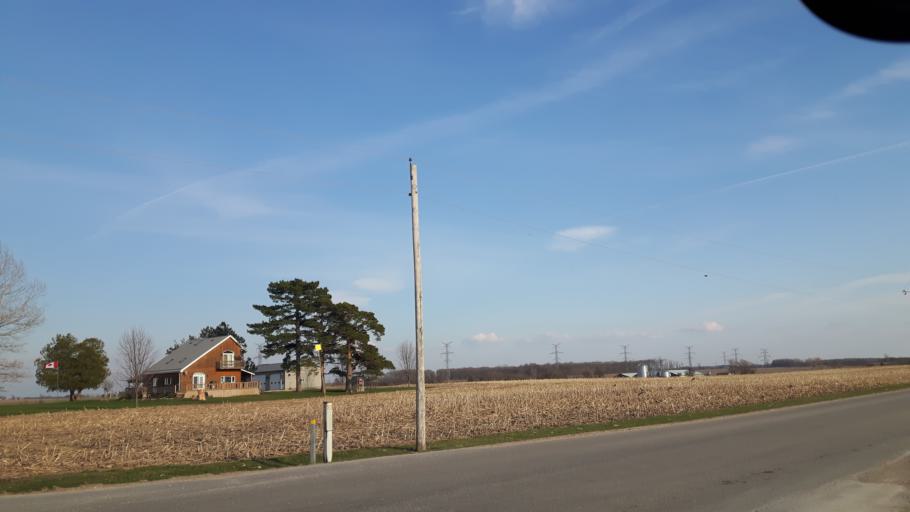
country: CA
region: Ontario
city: Goderich
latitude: 43.6985
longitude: -81.6645
